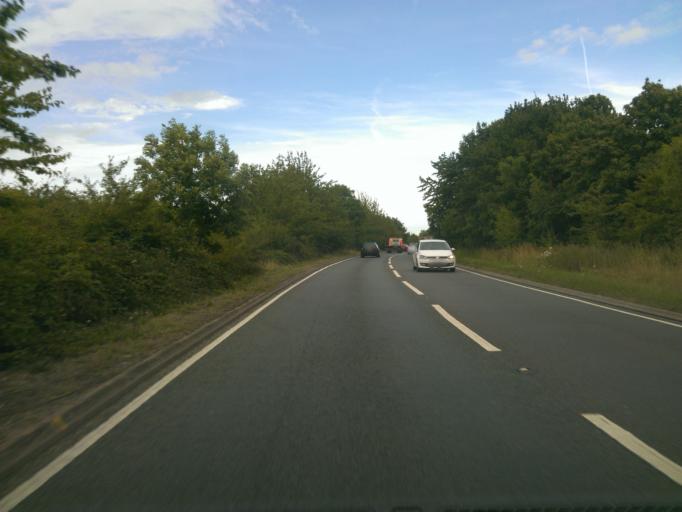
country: GB
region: England
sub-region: Essex
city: Coggeshall
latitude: 51.8820
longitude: 0.6824
